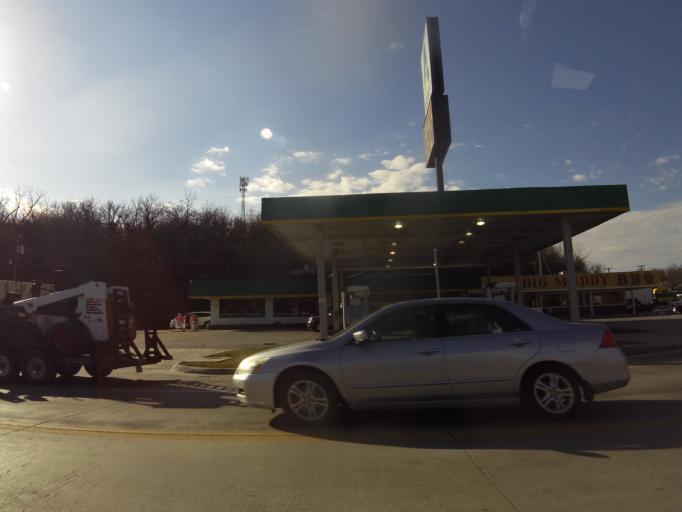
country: US
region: Missouri
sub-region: Marion County
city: Hannibal
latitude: 39.7053
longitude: -91.3888
